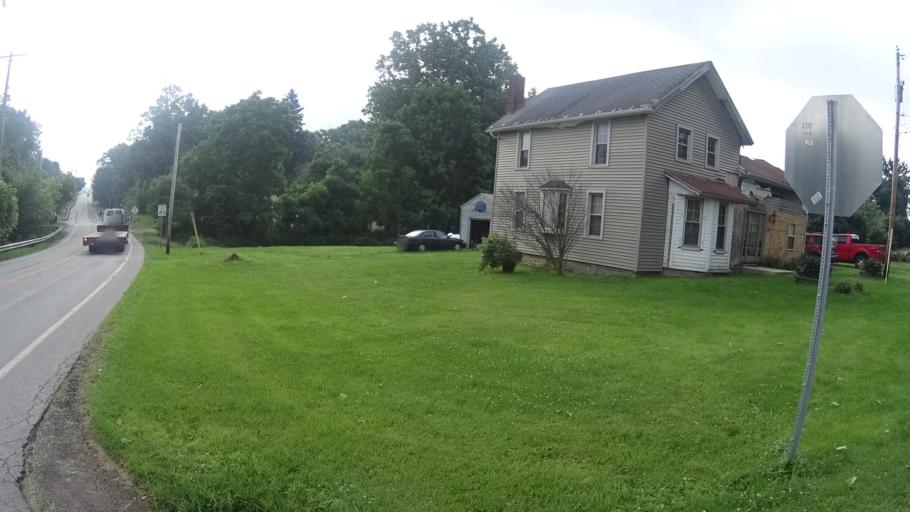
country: US
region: Ohio
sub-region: Erie County
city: Milan
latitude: 41.3027
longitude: -82.5143
